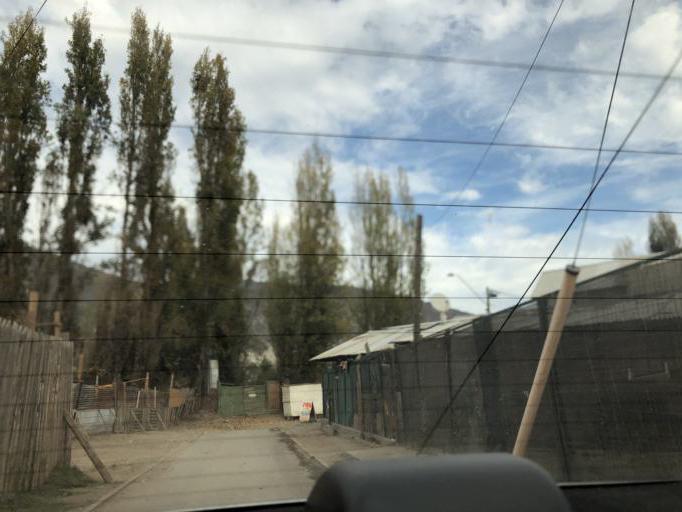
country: CL
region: Santiago Metropolitan
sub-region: Provincia de Cordillera
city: Puente Alto
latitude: -33.6117
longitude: -70.5169
